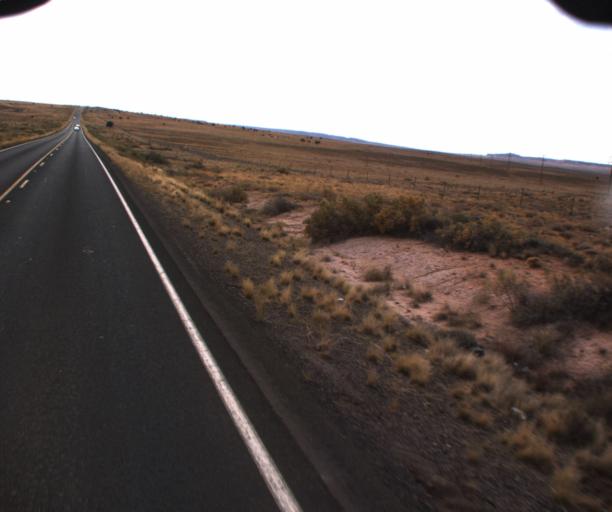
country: US
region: Arizona
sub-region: Apache County
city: Ganado
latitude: 35.8822
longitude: -109.6039
